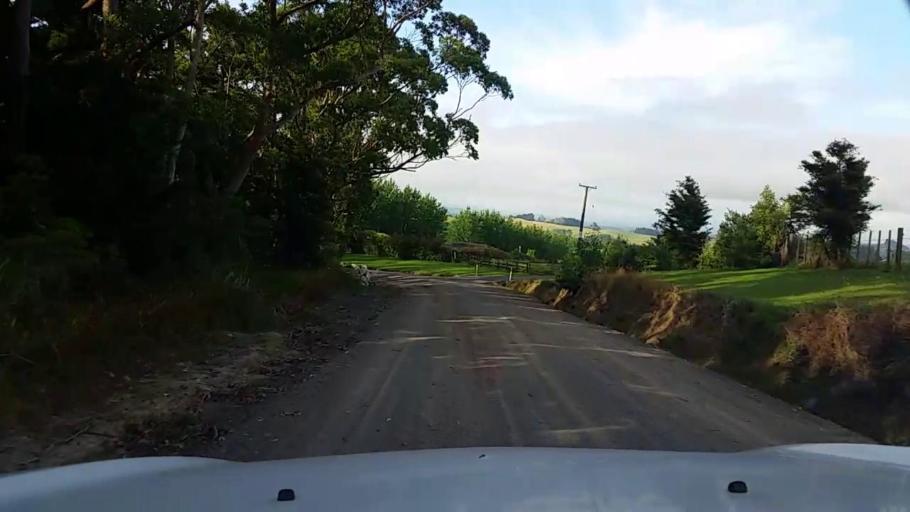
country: NZ
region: Northland
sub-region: Whangarei
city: Maungatapere
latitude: -35.6702
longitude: 174.1752
